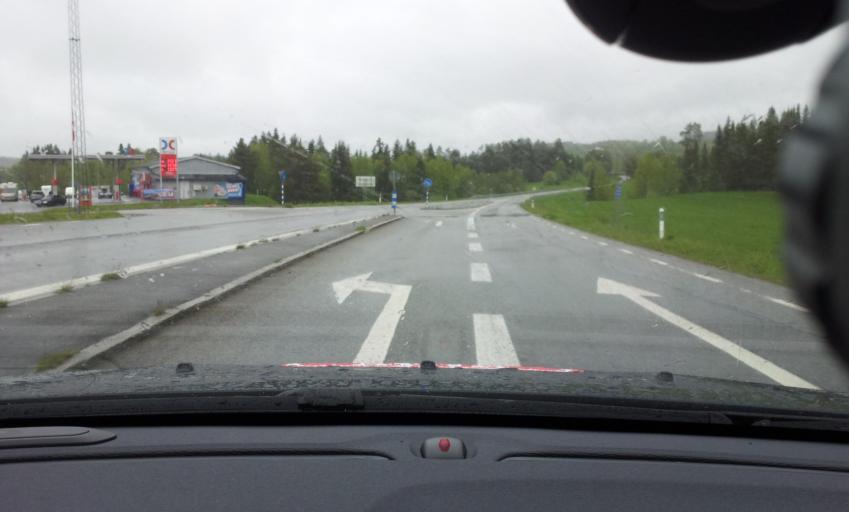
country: SE
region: Jaemtland
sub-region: Bergs Kommun
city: Hoverberg
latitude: 62.7512
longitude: 14.4277
